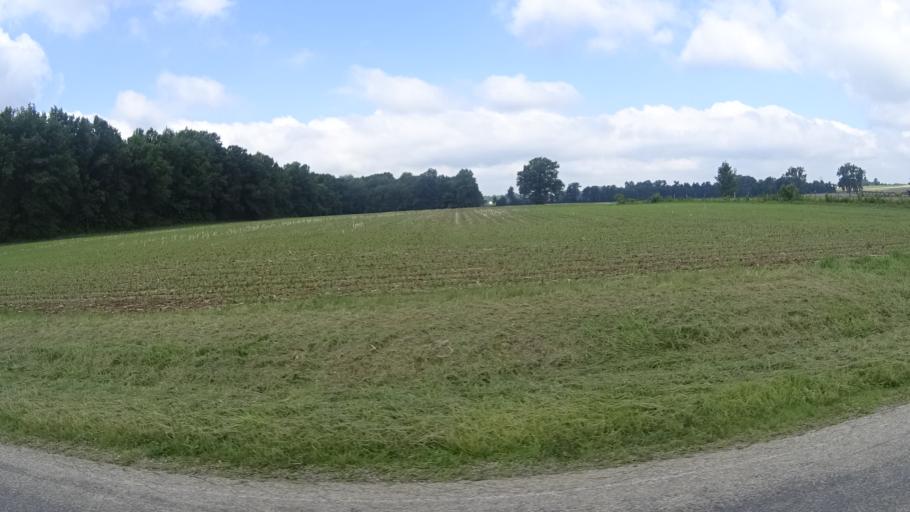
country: US
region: Ohio
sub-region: Huron County
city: Wakeman
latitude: 41.2991
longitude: -82.4429
